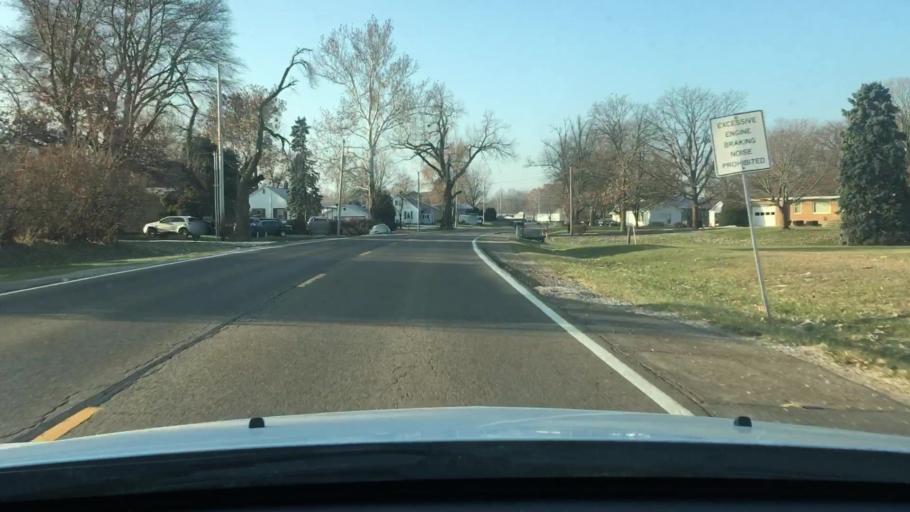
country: US
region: Illinois
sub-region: Woodford County
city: Metamora
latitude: 40.7991
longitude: -89.3576
